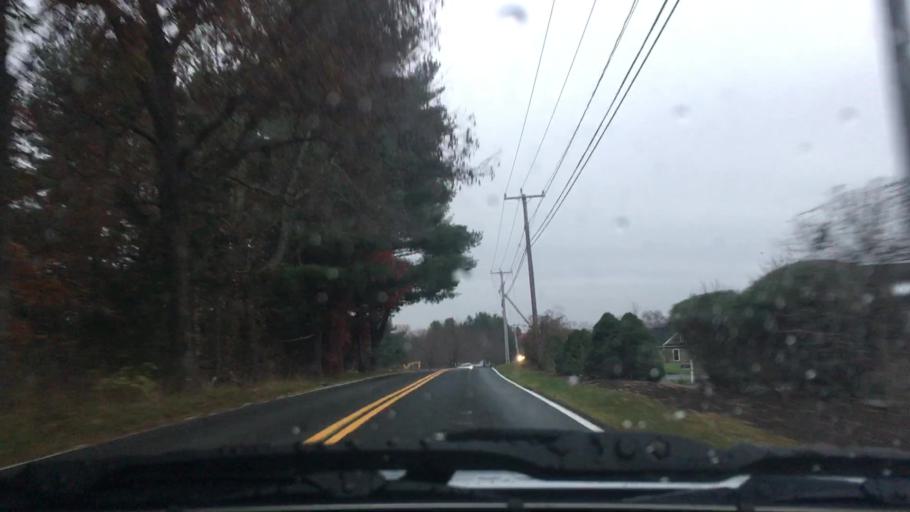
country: US
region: Massachusetts
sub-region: Hampden County
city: Southwick
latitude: 42.0834
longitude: -72.7724
